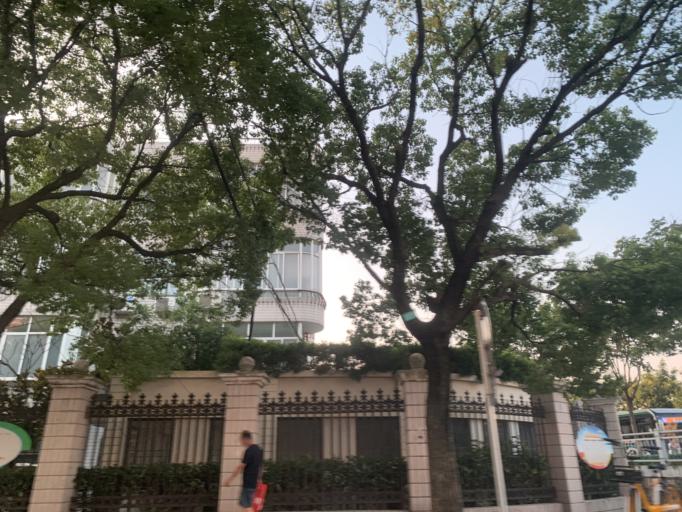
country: CN
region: Shanghai Shi
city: Huamu
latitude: 31.1873
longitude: 121.5495
